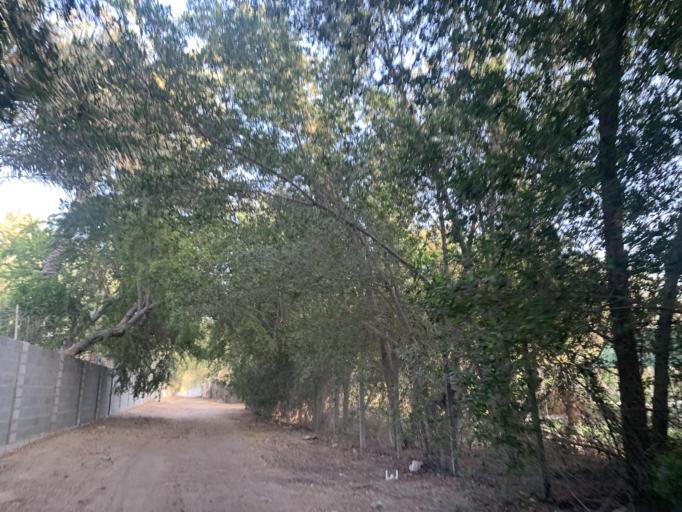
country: BH
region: Manama
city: Jidd Hafs
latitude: 26.2215
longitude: 50.5281
